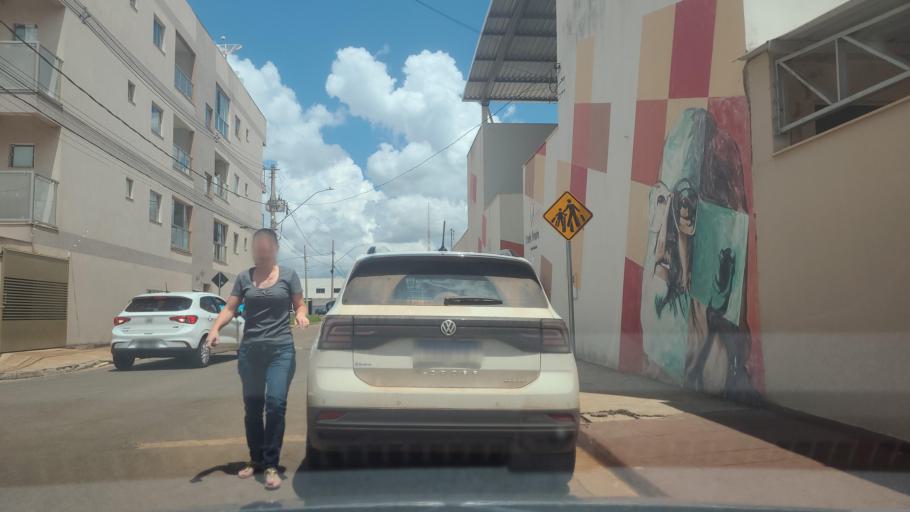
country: BR
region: Minas Gerais
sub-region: Carmo Do Paranaiba
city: Carmo do Paranaiba
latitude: -19.2005
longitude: -46.2364
